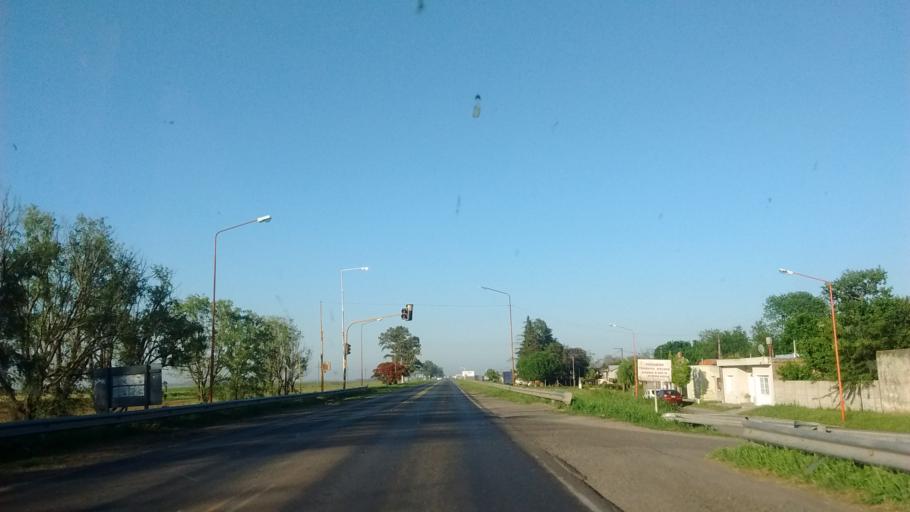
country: AR
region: Santa Fe
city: Venado Tuerto
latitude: -33.6490
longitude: -61.8621
